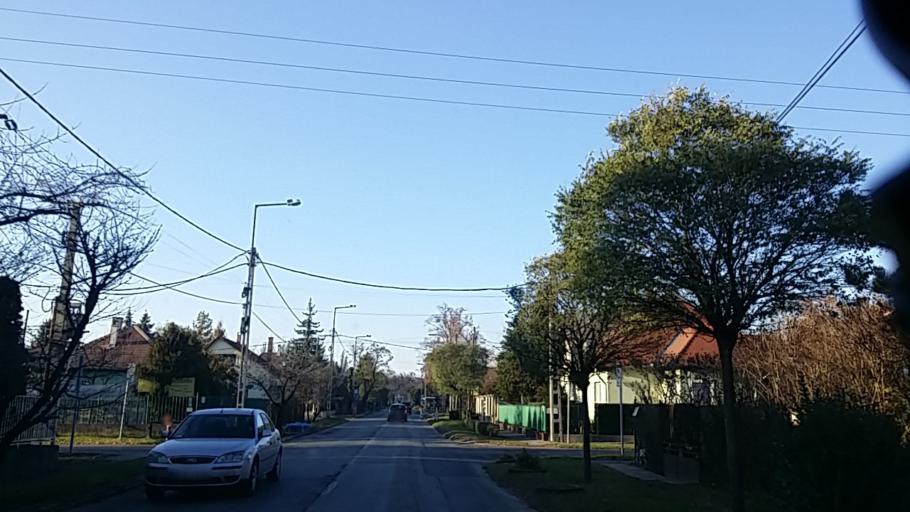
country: HU
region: Budapest
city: Budapest XVI. keruelet
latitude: 47.5053
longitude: 19.2122
